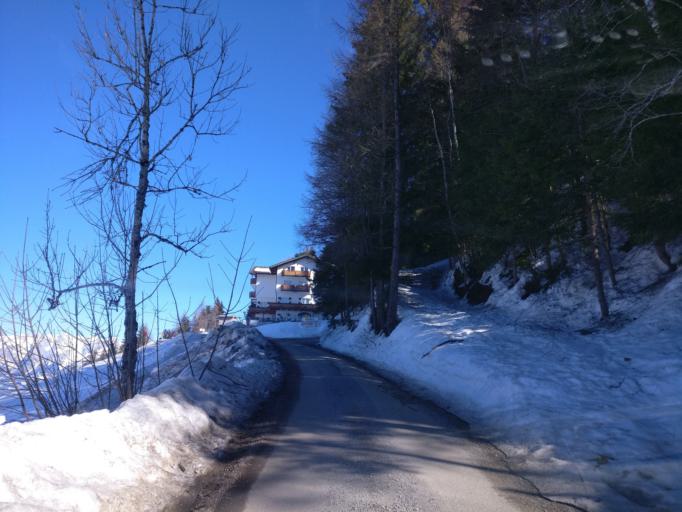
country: AT
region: Salzburg
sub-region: Politischer Bezirk Sankt Johann im Pongau
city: Sankt Johann im Pongau
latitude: 47.3397
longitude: 13.2248
